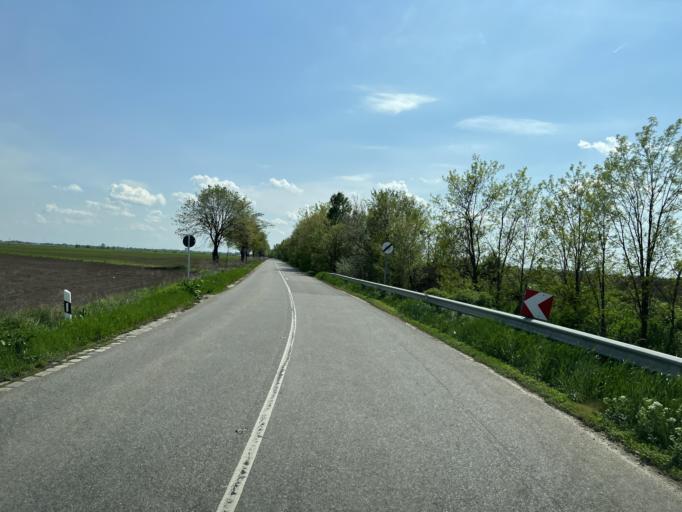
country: HU
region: Pest
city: Cegled
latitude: 47.2256
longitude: 19.7704
